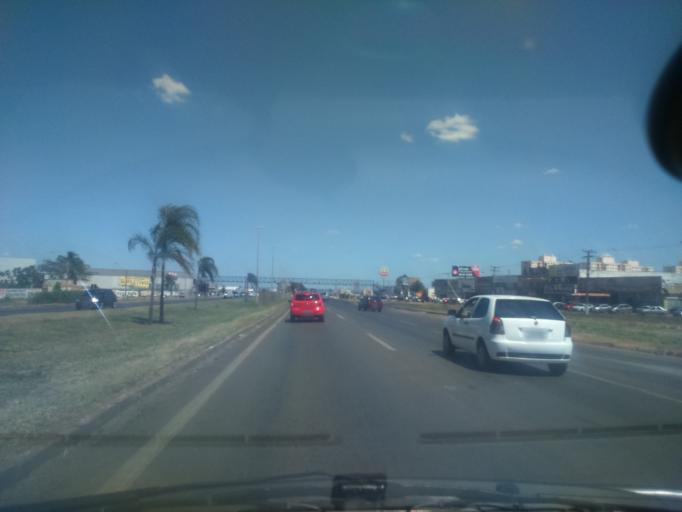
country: BR
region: Goias
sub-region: Luziania
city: Luziania
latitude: -16.0754
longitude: -47.9856
